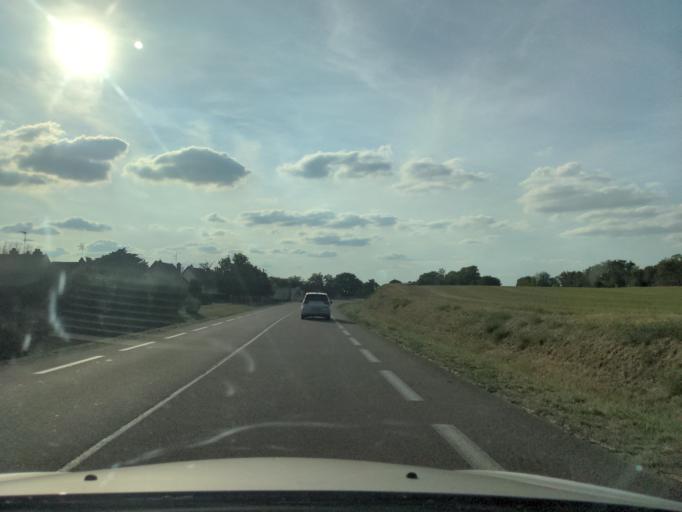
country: FR
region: Bourgogne
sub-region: Departement de la Cote-d'Or
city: Neuilly-les-Dijon
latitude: 47.2831
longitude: 5.1034
